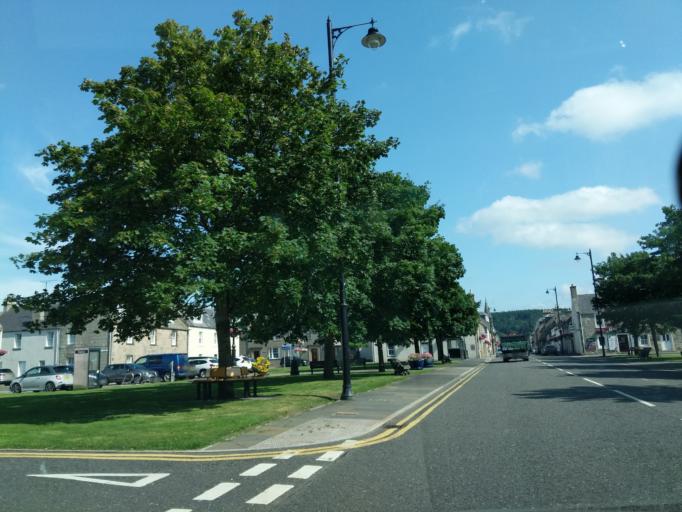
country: GB
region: Scotland
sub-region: Moray
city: Fochabers
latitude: 57.6144
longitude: -3.0981
